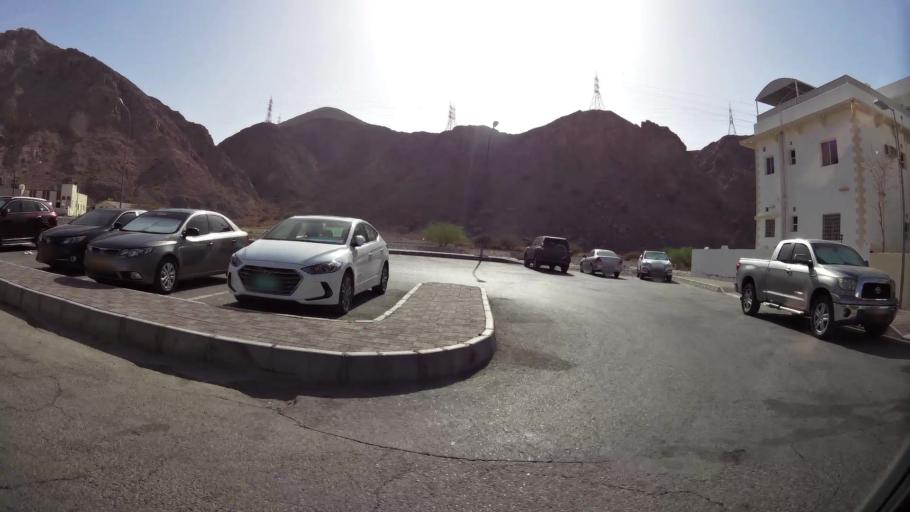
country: OM
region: Muhafazat Masqat
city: Muscat
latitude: 23.5863
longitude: 58.5153
